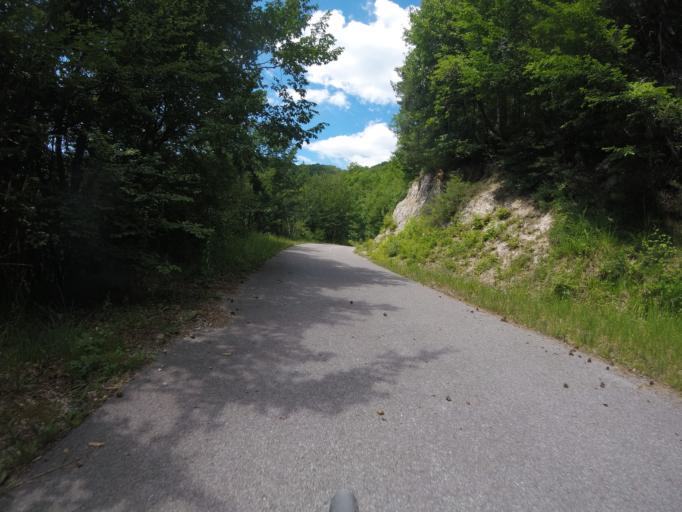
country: SI
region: Kostanjevica na Krki
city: Kostanjevica na Krki
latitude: 45.7713
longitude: 15.4135
